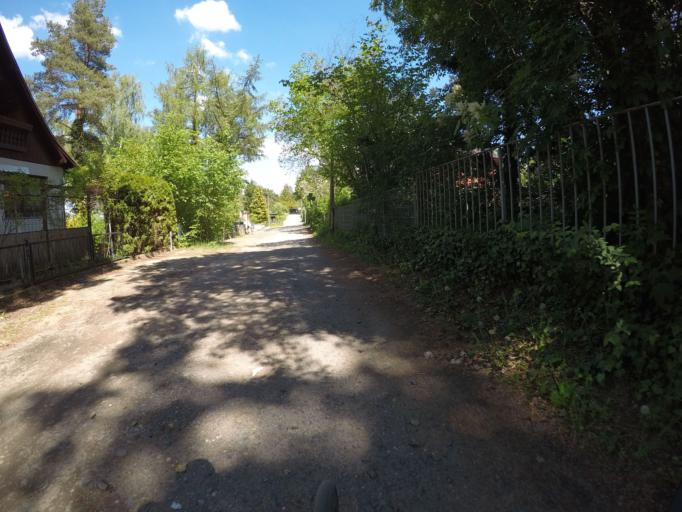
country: DE
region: Brandenburg
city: Michendorf
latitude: 52.3396
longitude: 12.9824
